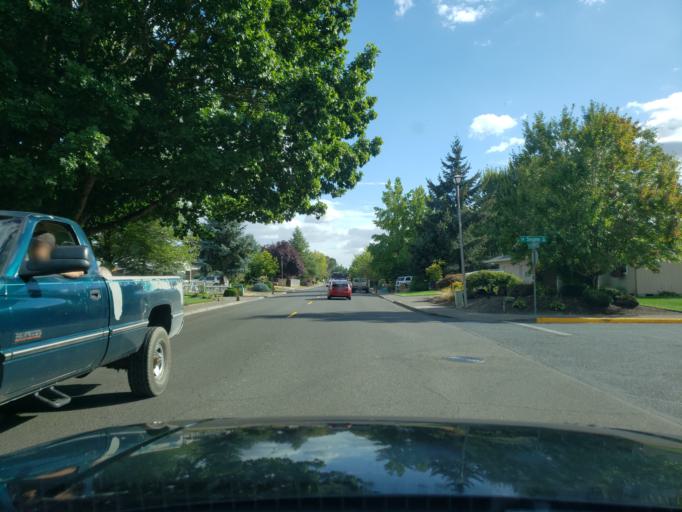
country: US
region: Oregon
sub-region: Yamhill County
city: McMinnville
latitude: 45.2064
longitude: -123.2196
